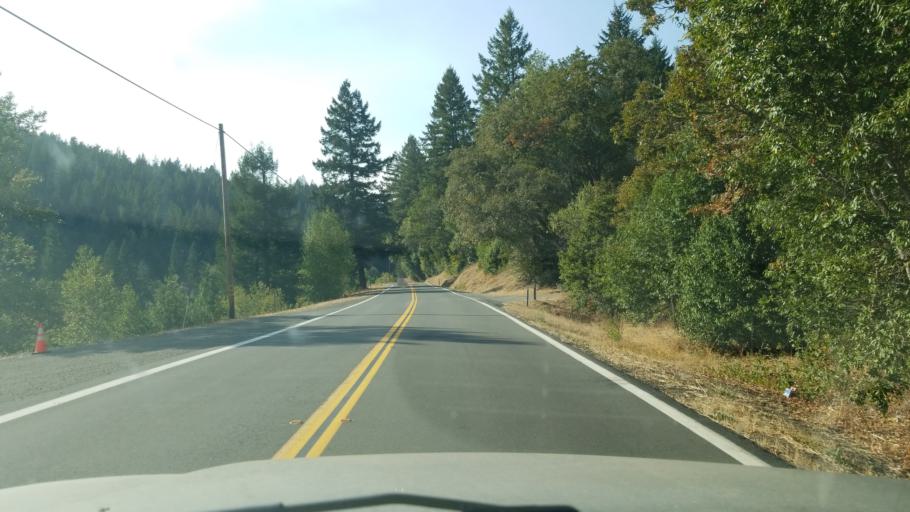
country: US
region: California
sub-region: Humboldt County
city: Redway
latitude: 40.1953
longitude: -123.7706
